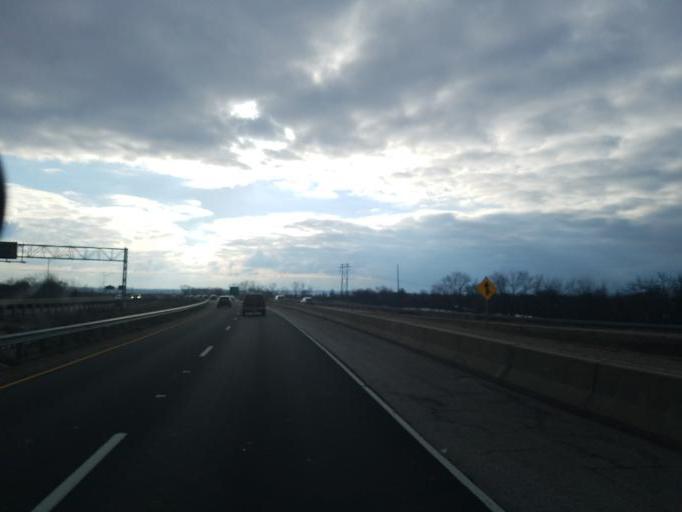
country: US
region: Illinois
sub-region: Madison County
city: Mitchell
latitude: 38.7587
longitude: -90.0922
